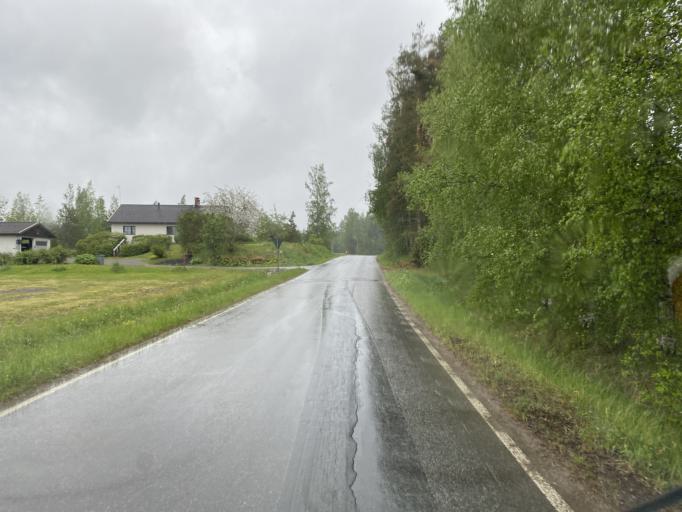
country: FI
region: Haeme
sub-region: Forssa
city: Humppila
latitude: 61.0962
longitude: 23.3167
